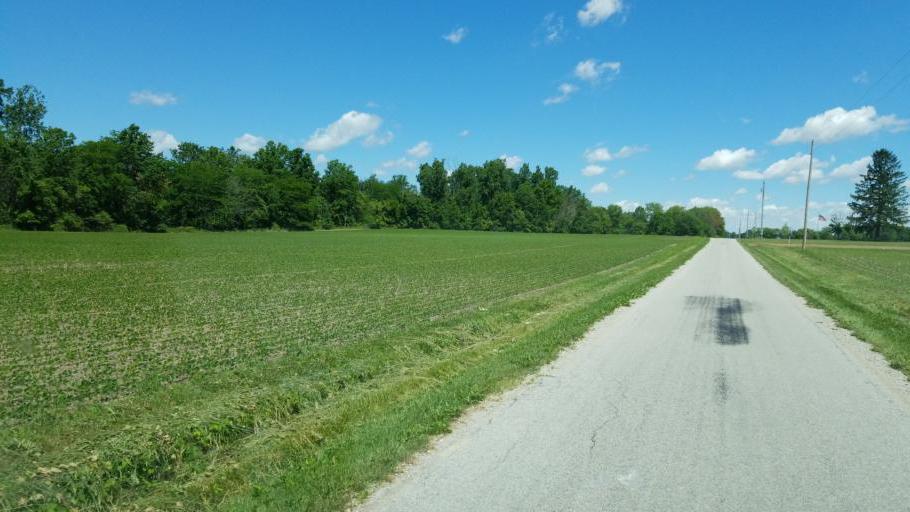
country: US
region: Ohio
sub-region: Crawford County
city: Bucyrus
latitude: 40.6755
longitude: -82.9389
